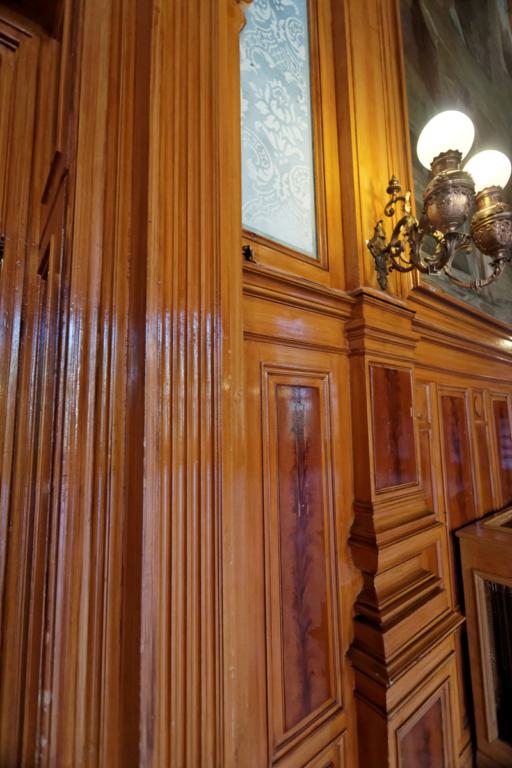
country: CZ
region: Karlovarsky
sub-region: Okres Karlovy Vary
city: Karlovy Vary
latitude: 50.2189
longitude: 12.8814
